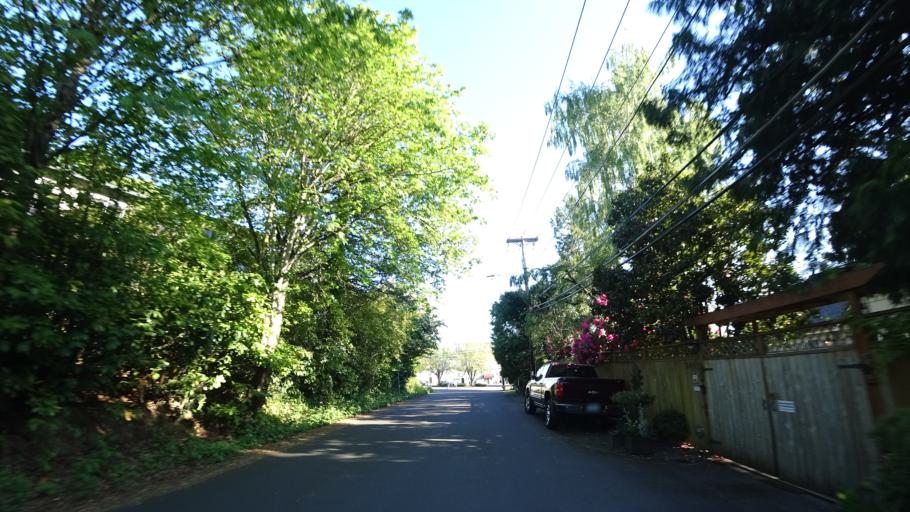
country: US
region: Oregon
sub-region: Washington County
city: West Slope
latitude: 45.4996
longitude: -122.7666
